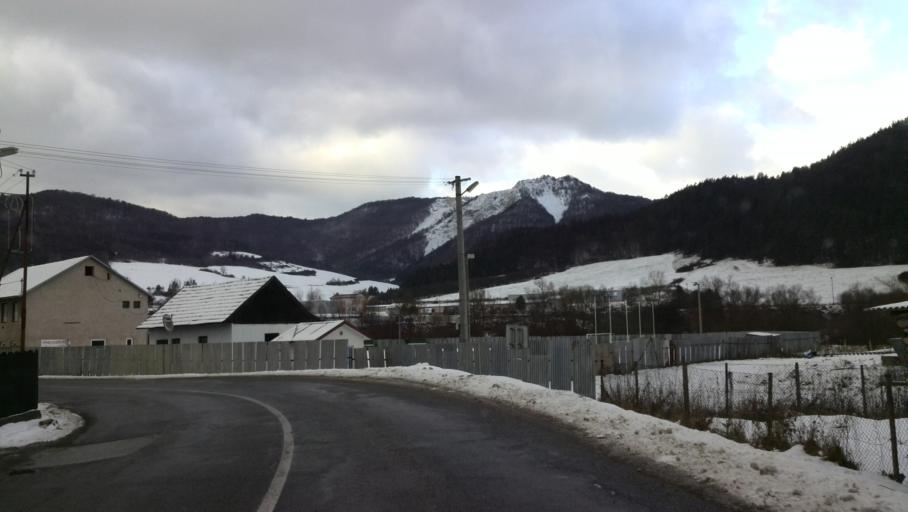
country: SK
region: Kosicky
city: Gelnica
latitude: 48.8736
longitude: 20.9909
